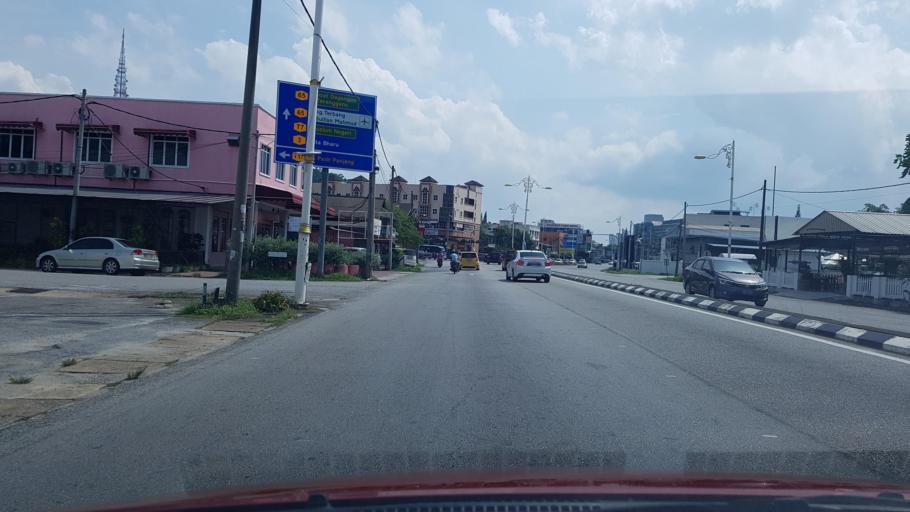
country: MY
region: Terengganu
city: Kuala Terengganu
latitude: 5.3133
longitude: 103.1413
